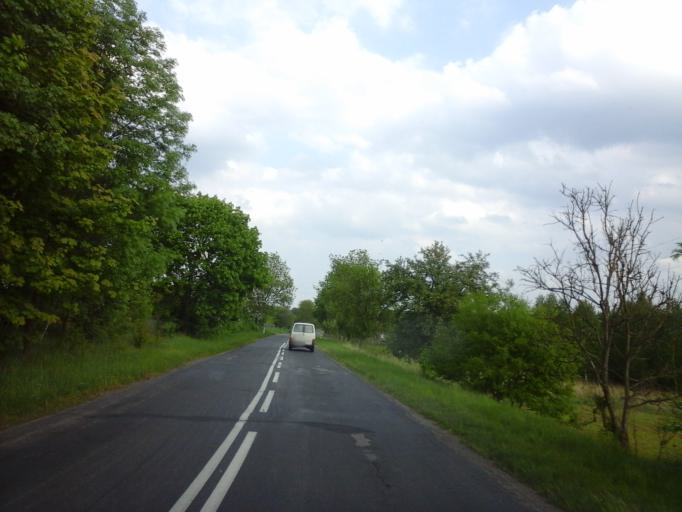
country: PL
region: West Pomeranian Voivodeship
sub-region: Powiat mysliborski
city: Barlinek
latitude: 52.9689
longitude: 15.2626
